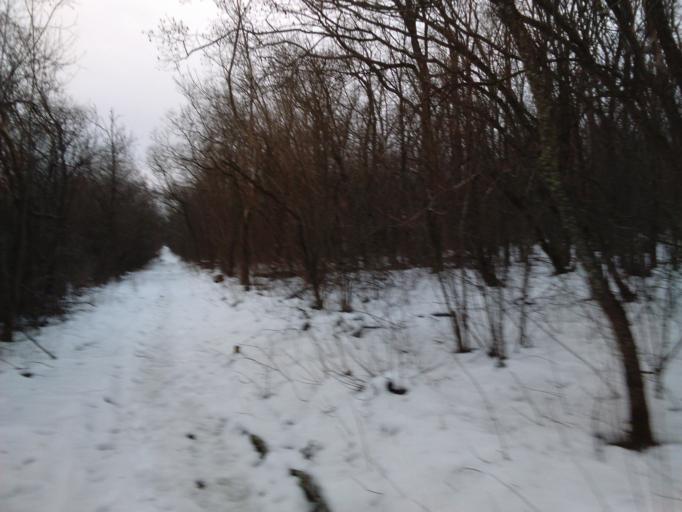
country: RU
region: Rostov
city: Temernik
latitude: 47.3511
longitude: 39.7395
